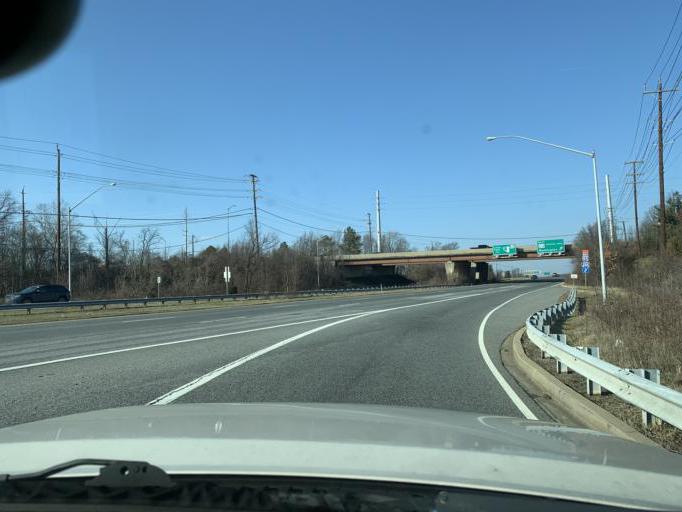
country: US
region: Maryland
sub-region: Prince George's County
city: Largo
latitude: 38.8971
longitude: -76.8311
